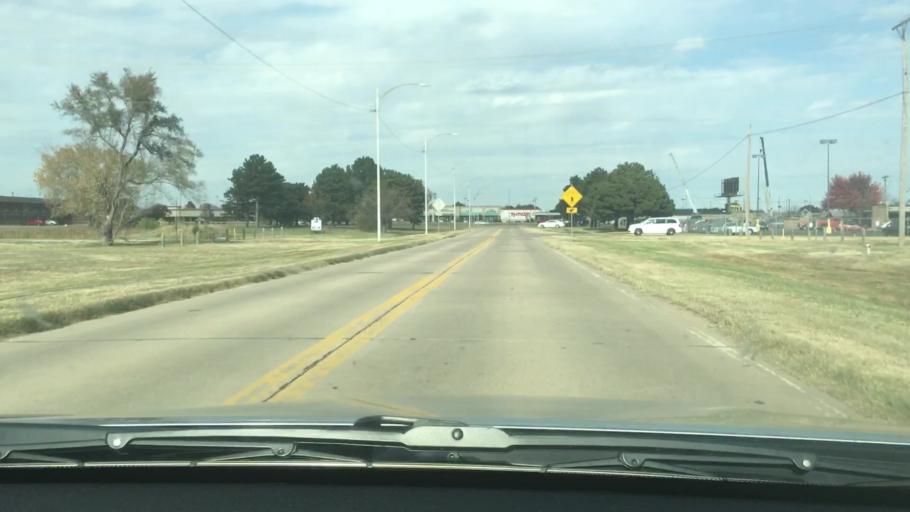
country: US
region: Kansas
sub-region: Sedgwick County
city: Wichita
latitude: 37.6697
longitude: -97.4212
